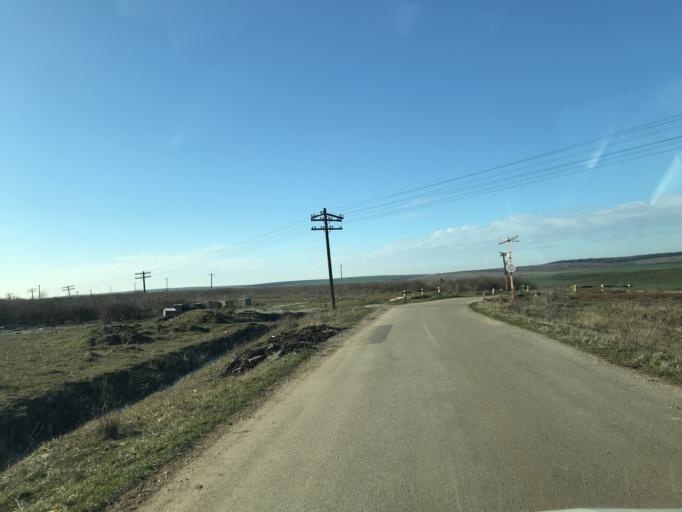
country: RO
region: Olt
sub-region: Comuna Piatra Olt
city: Piatra Olt
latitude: 44.3575
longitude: 24.2451
